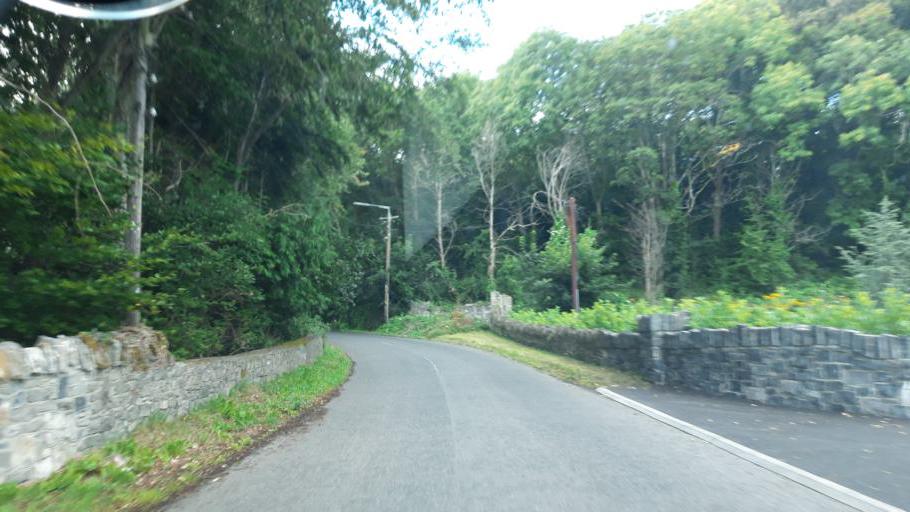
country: IE
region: Leinster
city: Lucan
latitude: 53.3597
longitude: -6.4523
